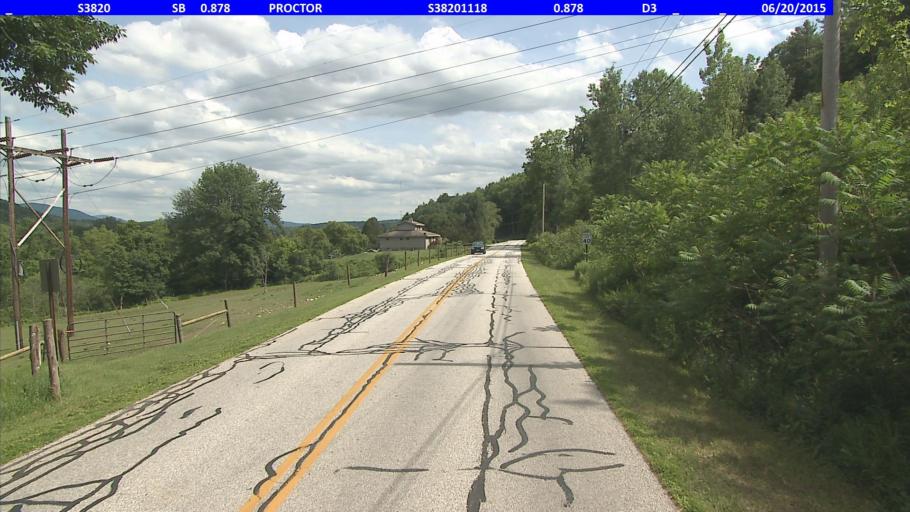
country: US
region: Vermont
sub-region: Rutland County
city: West Rutland
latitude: 43.6224
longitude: -73.0340
